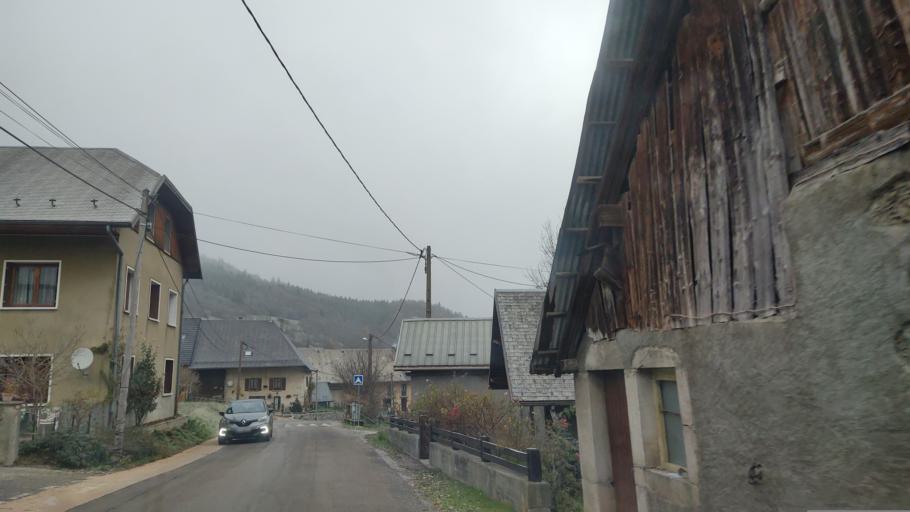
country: FR
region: Rhone-Alpes
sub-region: Departement de la Savoie
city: Coise-Saint-Jean-Pied-Gauthier
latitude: 45.5961
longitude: 6.1369
